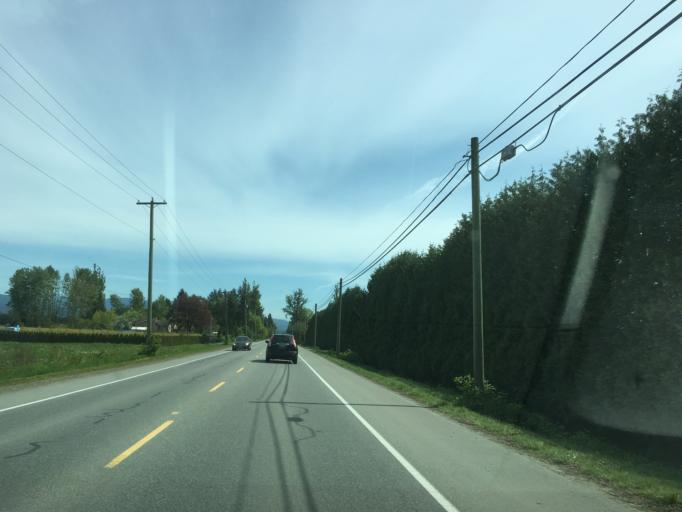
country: CA
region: British Columbia
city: Pitt Meadows
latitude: 49.2442
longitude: -122.7051
